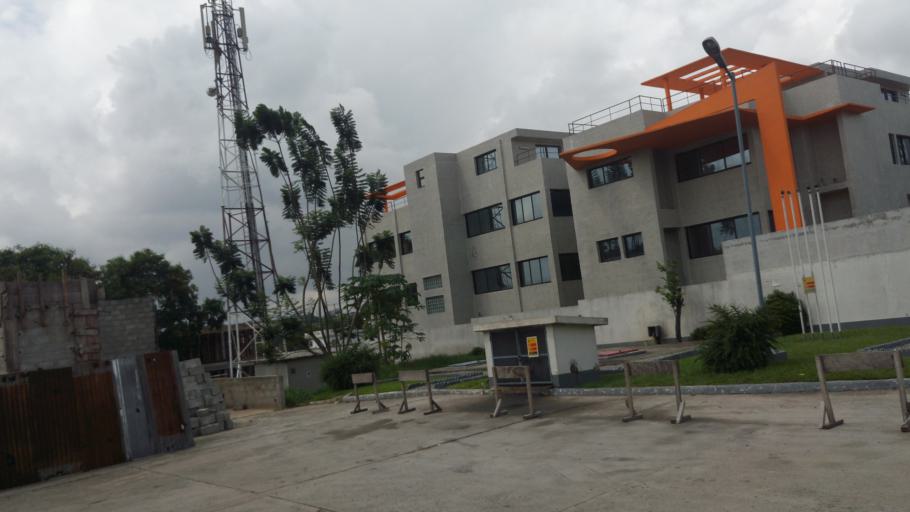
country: CI
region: Lagunes
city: Abidjan
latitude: 5.3545
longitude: -3.9954
